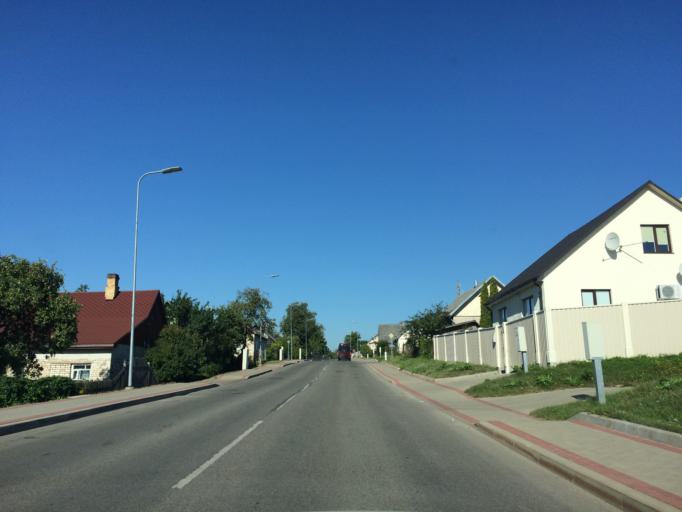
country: LV
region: Rezekne
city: Rezekne
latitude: 56.5117
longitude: 27.3488
